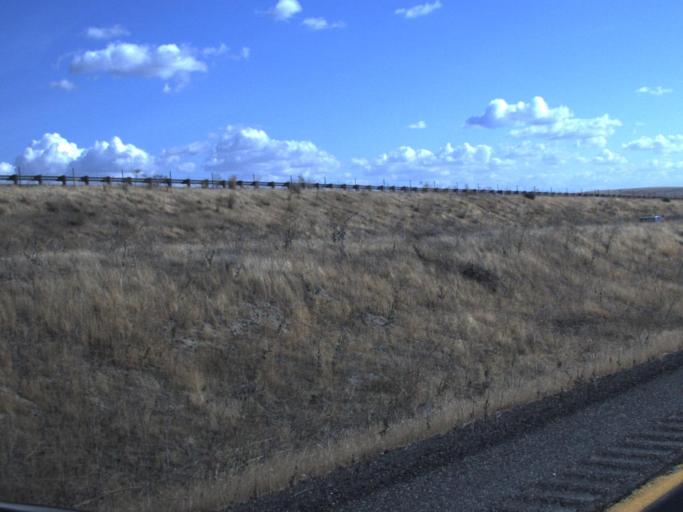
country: US
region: Washington
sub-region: Benton County
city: Highland
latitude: 46.0424
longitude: -119.2246
